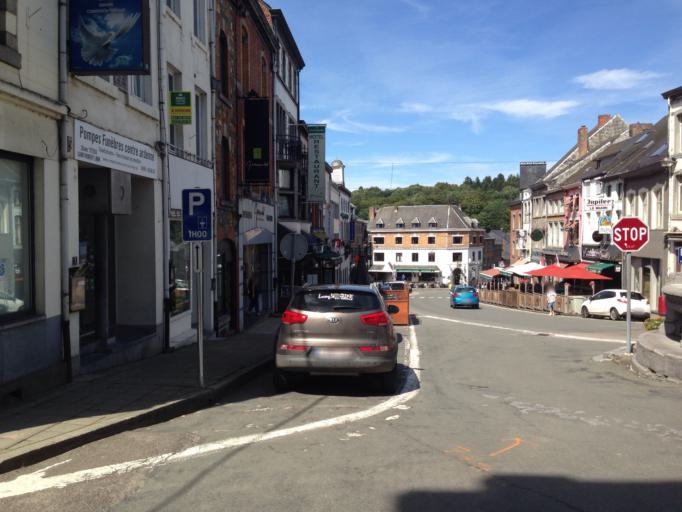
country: BE
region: Wallonia
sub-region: Province du Luxembourg
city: Saint-Hubert
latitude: 50.0252
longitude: 5.3738
